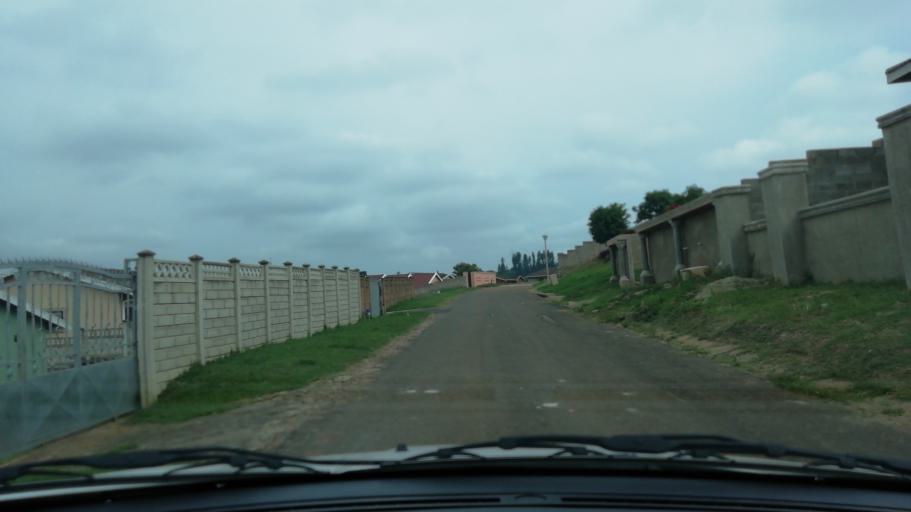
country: ZA
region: KwaZulu-Natal
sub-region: uThungulu District Municipality
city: Empangeni
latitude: -28.7383
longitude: 31.8801
